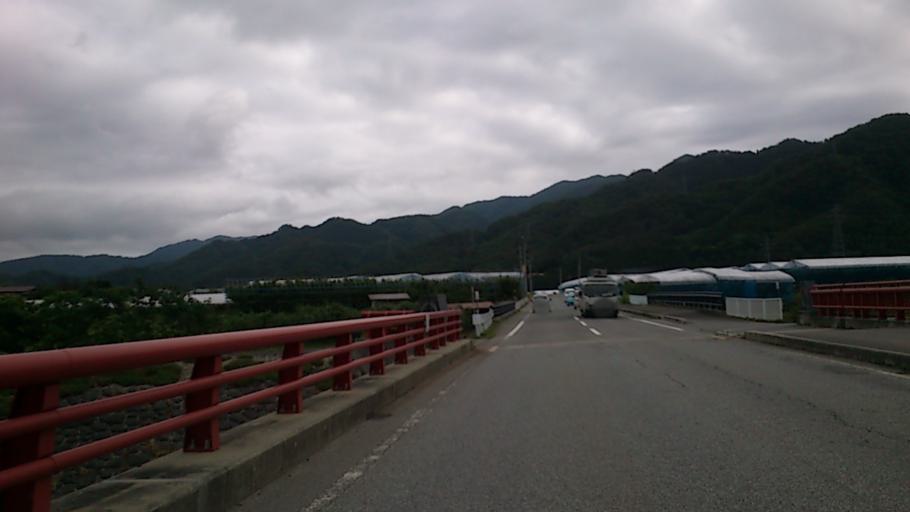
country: JP
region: Yamagata
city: Tendo
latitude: 38.3105
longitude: 140.4074
